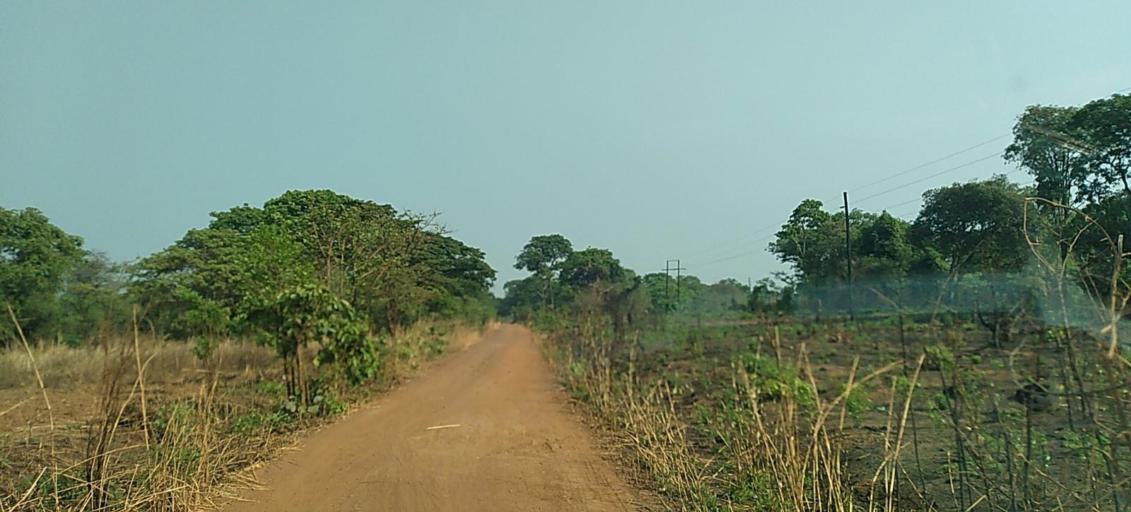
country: ZM
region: Copperbelt
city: Chingola
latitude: -12.8416
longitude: 27.5461
